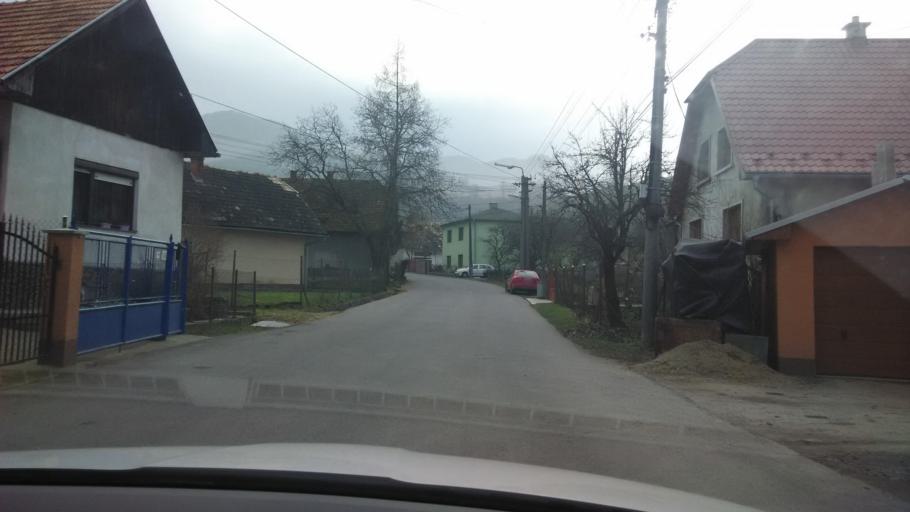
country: SK
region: Banskobystricky
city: Nova Bana
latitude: 48.4265
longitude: 18.6852
